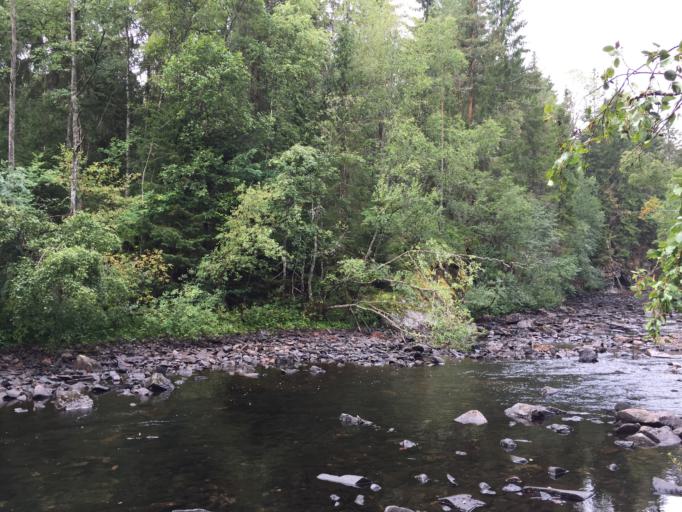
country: NO
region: Akershus
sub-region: Baerum
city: Lysaker
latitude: 60.0178
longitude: 10.6185
